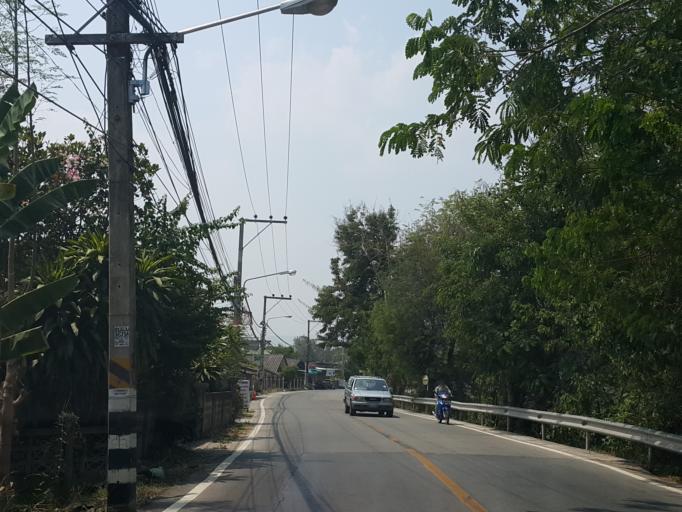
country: TH
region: Chiang Mai
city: Chiang Mai
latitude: 18.7372
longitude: 98.9826
